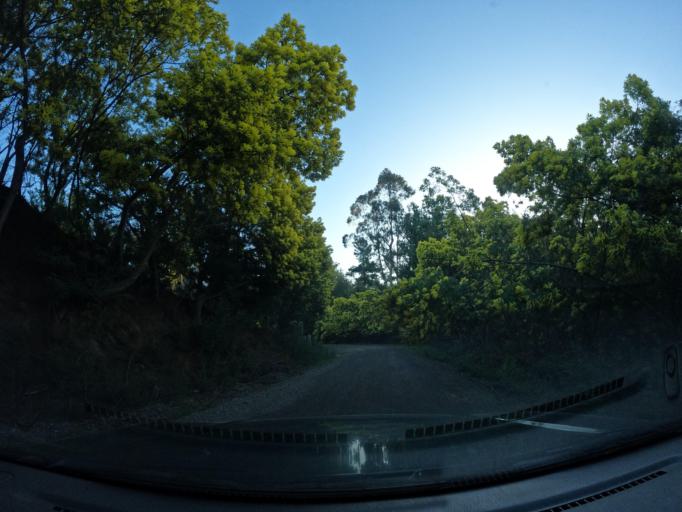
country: CL
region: Biobio
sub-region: Provincia de Concepcion
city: Chiguayante
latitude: -37.0161
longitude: -72.8387
